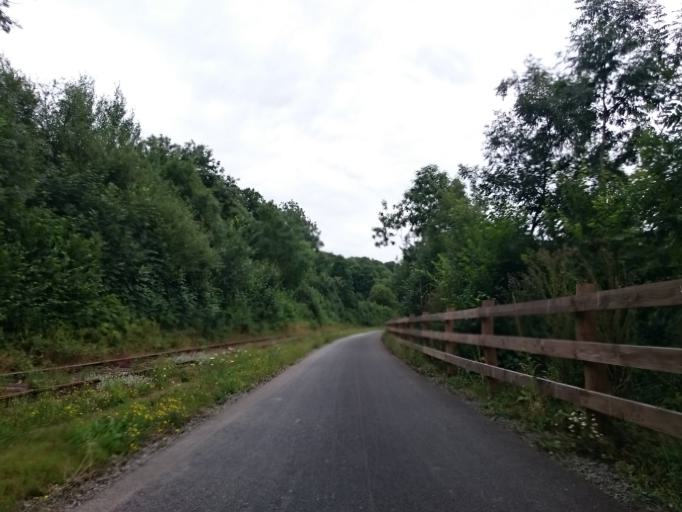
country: FR
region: Lower Normandy
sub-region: Departement du Calvados
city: Sainte-Honorine-du-Fay
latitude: 49.0497
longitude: -0.4581
